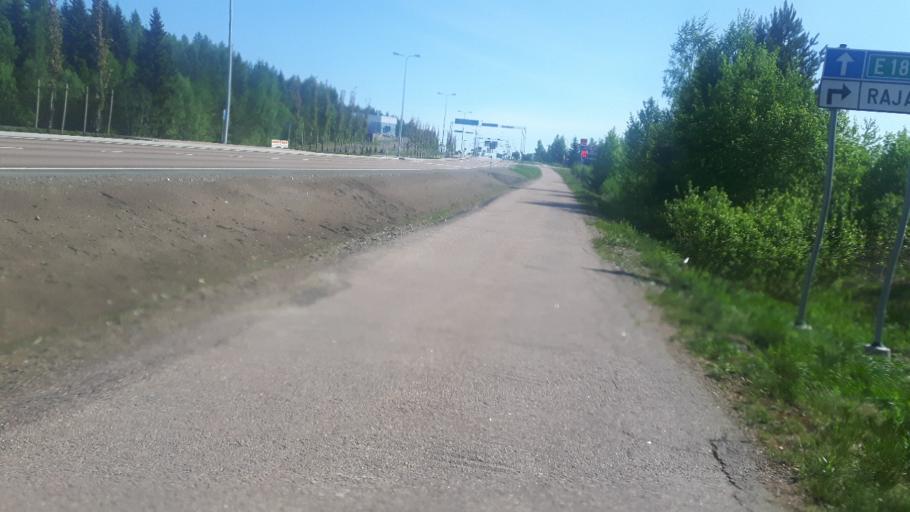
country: FI
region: Kymenlaakso
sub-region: Kotka-Hamina
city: Virojoki
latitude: 60.6011
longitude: 27.8347
